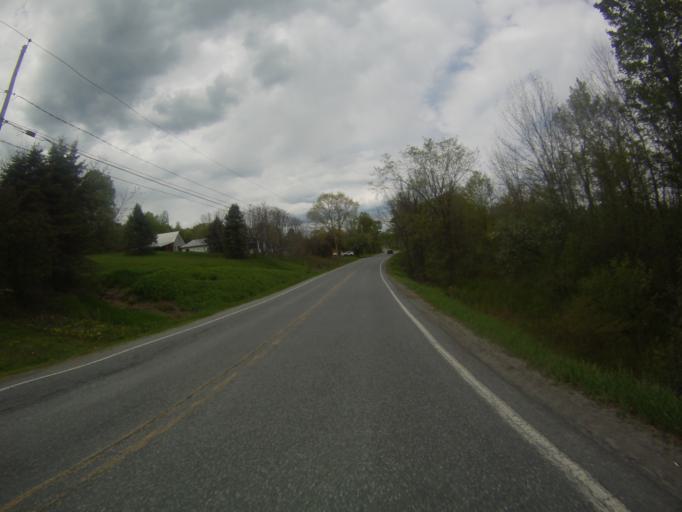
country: US
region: New York
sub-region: Essex County
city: Port Henry
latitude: 44.0347
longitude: -73.5031
